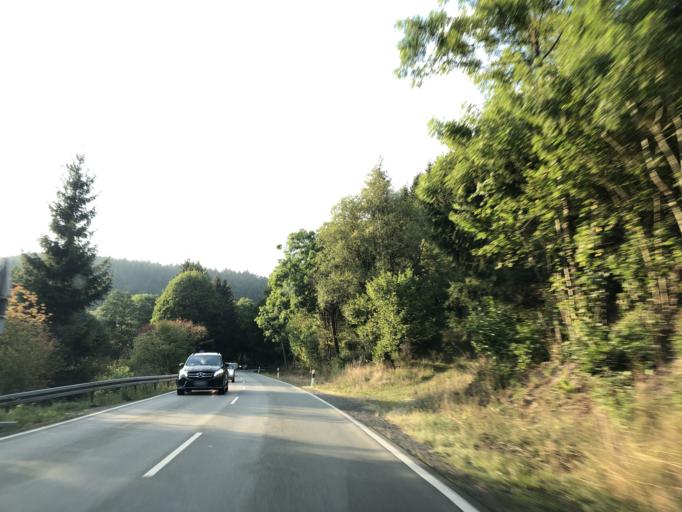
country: DE
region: North Rhine-Westphalia
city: Hallenberg
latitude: 51.1383
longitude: 8.5887
